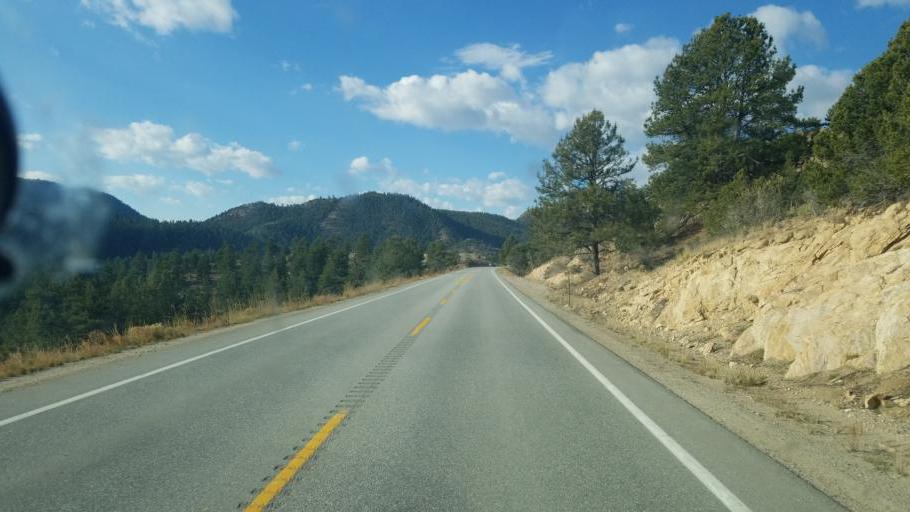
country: US
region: Colorado
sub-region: Chaffee County
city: Buena Vista
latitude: 38.8458
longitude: -105.9889
